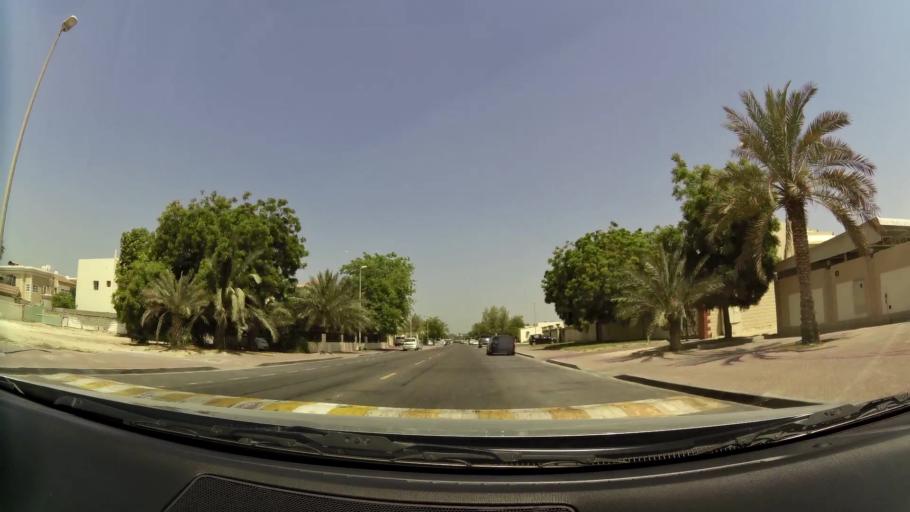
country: AE
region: Dubai
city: Dubai
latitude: 25.2128
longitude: 55.2662
